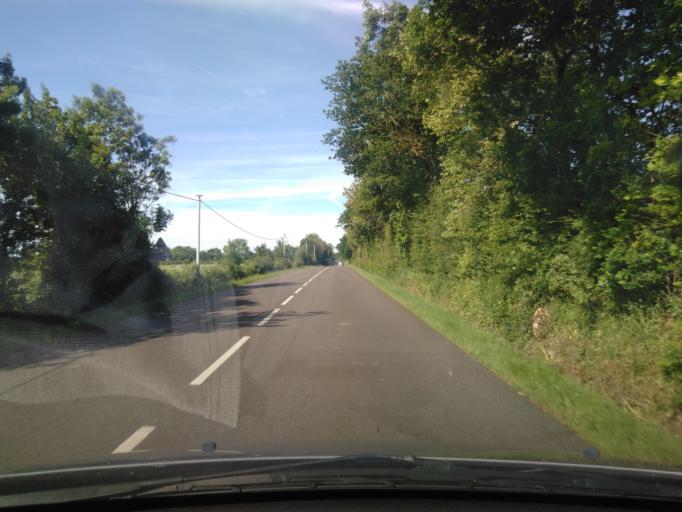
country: FR
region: Pays de la Loire
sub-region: Departement de la Vendee
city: Nieul-le-Dolent
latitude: 46.5519
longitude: -1.5257
